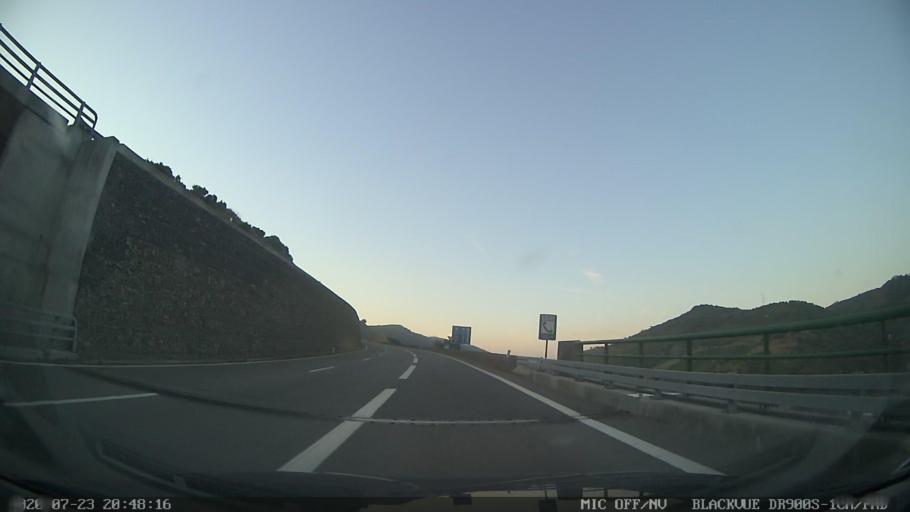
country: PT
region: Vila Real
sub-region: Peso da Regua
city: Peso da Regua
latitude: 41.1759
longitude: -7.7496
